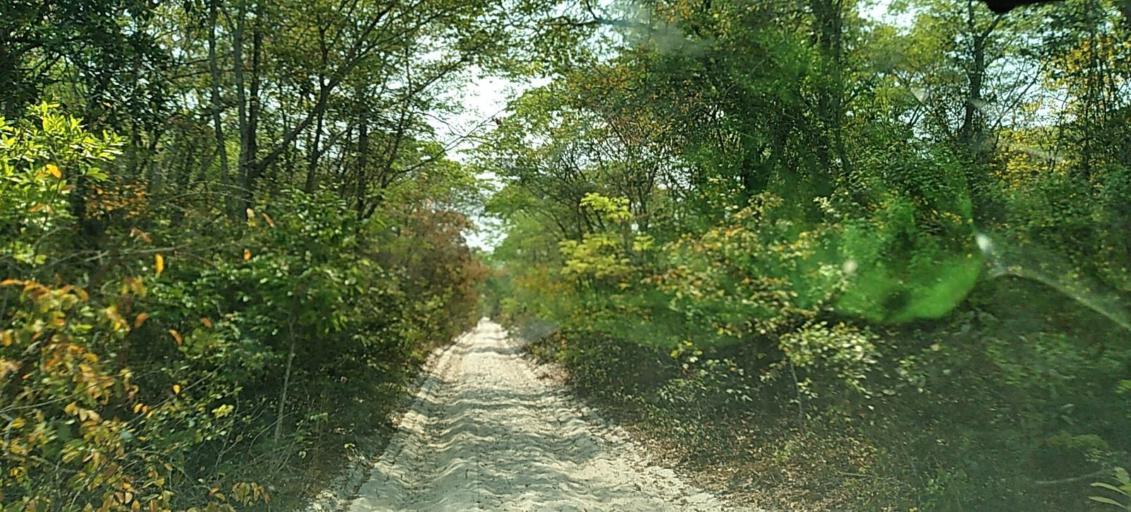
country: ZM
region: North-Western
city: Kabompo
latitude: -13.3903
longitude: 23.7823
